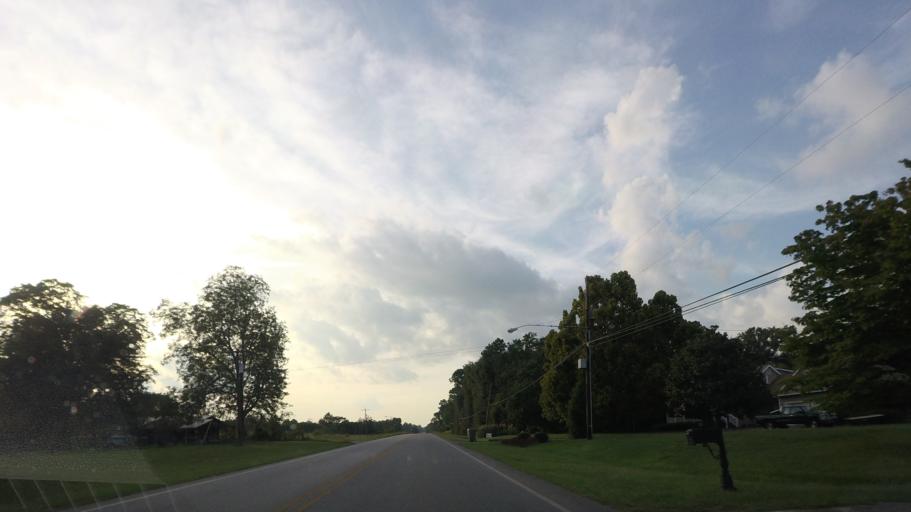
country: US
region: Georgia
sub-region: Wilkinson County
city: Gordon
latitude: 32.8883
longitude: -83.3504
